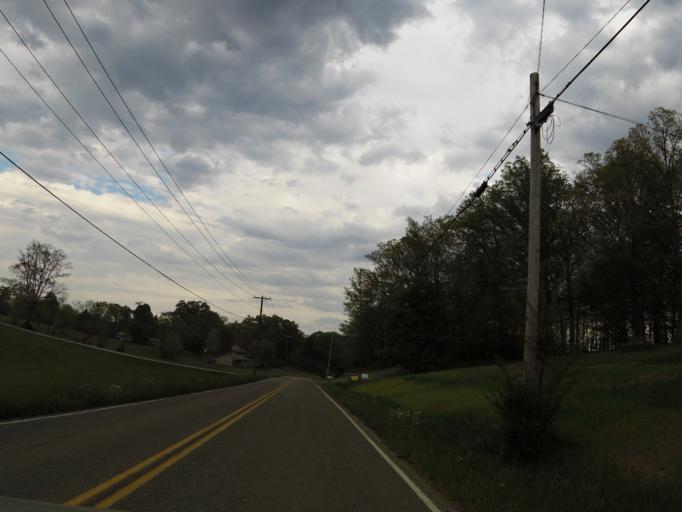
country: US
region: Tennessee
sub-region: Knox County
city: Knoxville
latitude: 35.8957
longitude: -83.8694
